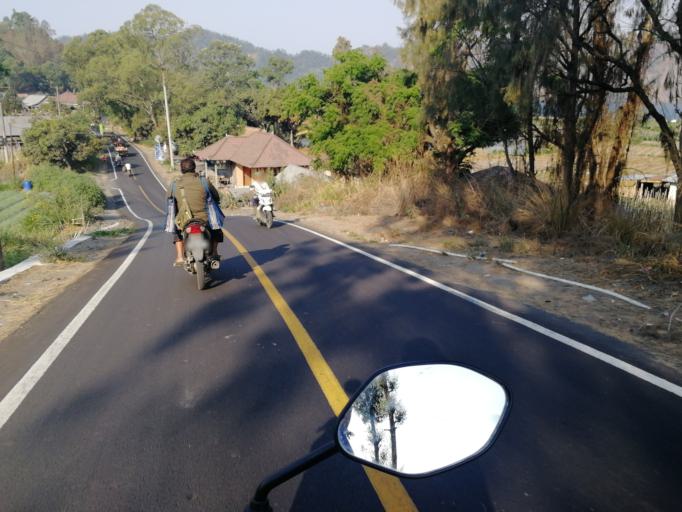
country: ID
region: Bali
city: Banjar Trunyan
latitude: -8.2427
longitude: 115.4022
